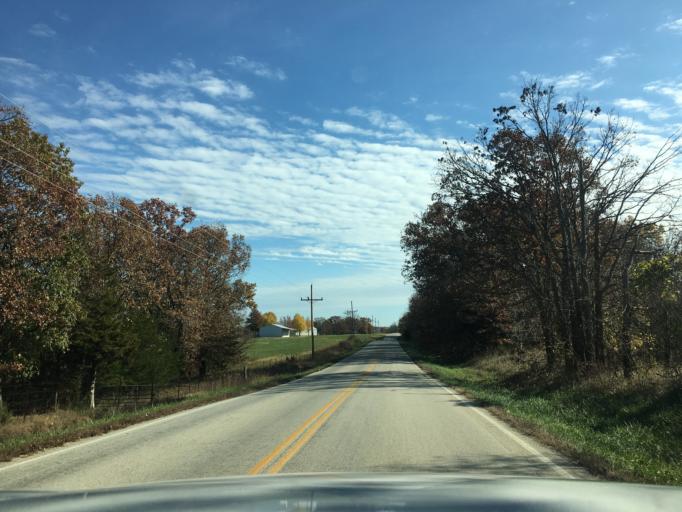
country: US
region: Missouri
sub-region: Maries County
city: Belle
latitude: 38.3578
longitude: -91.8041
